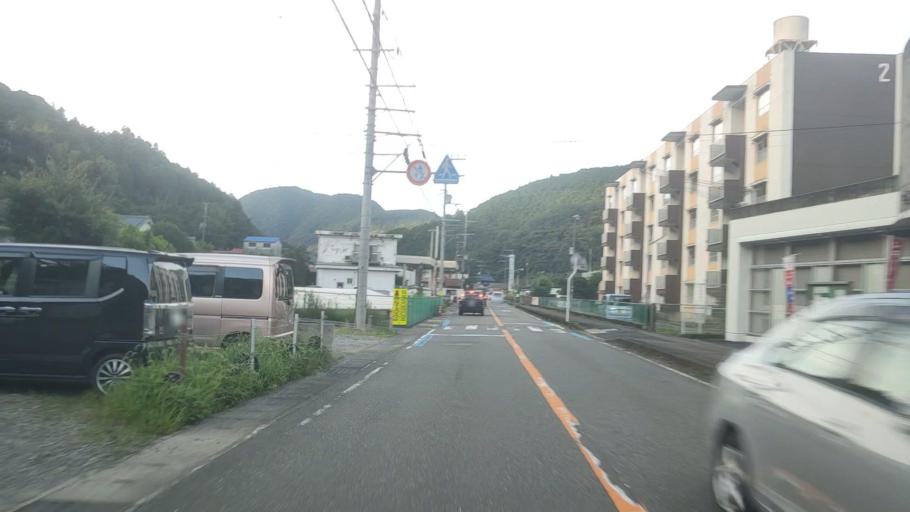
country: JP
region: Wakayama
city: Tanabe
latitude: 33.7924
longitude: 135.5171
